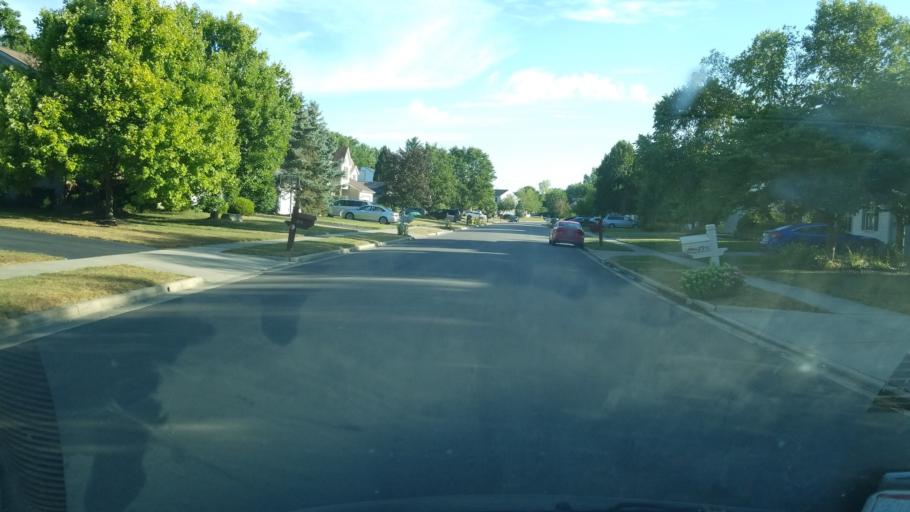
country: US
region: Ohio
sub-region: Delaware County
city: Lewis Center
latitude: 40.1698
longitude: -83.0035
